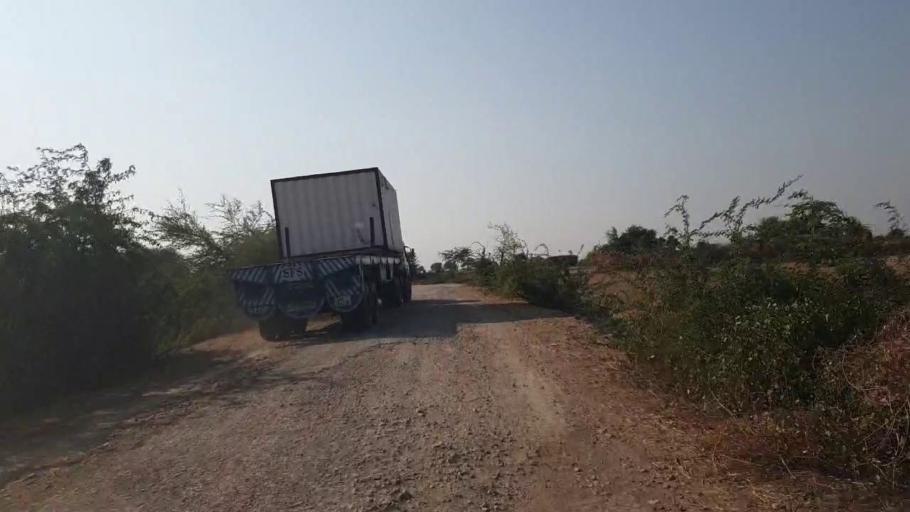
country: PK
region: Sindh
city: Matli
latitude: 24.9511
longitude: 68.6855
